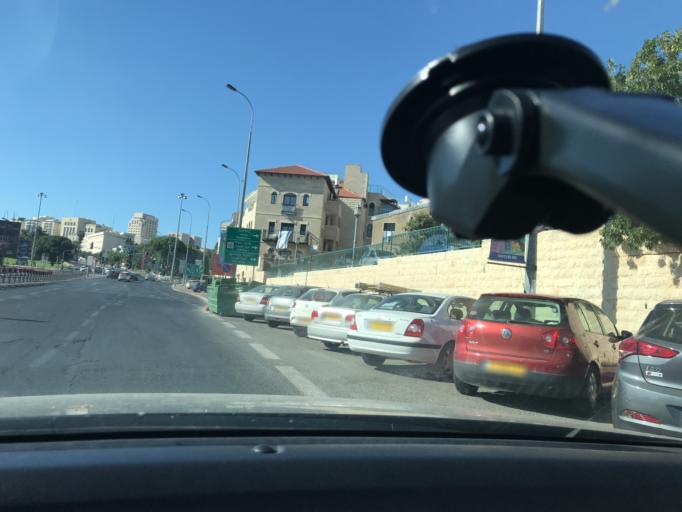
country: IL
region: Jerusalem
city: West Jerusalem
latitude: 31.7815
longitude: 35.2086
